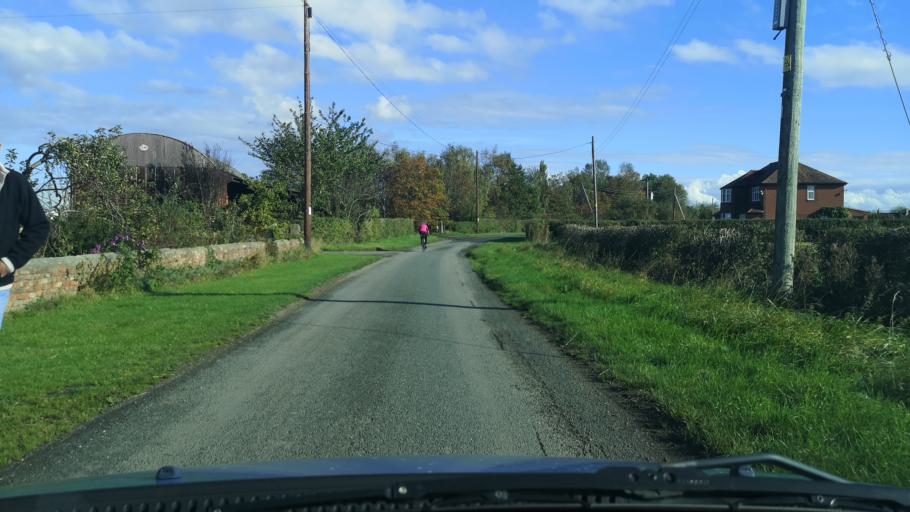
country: GB
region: England
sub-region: Doncaster
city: Fenwick
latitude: 53.6382
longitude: -1.1147
